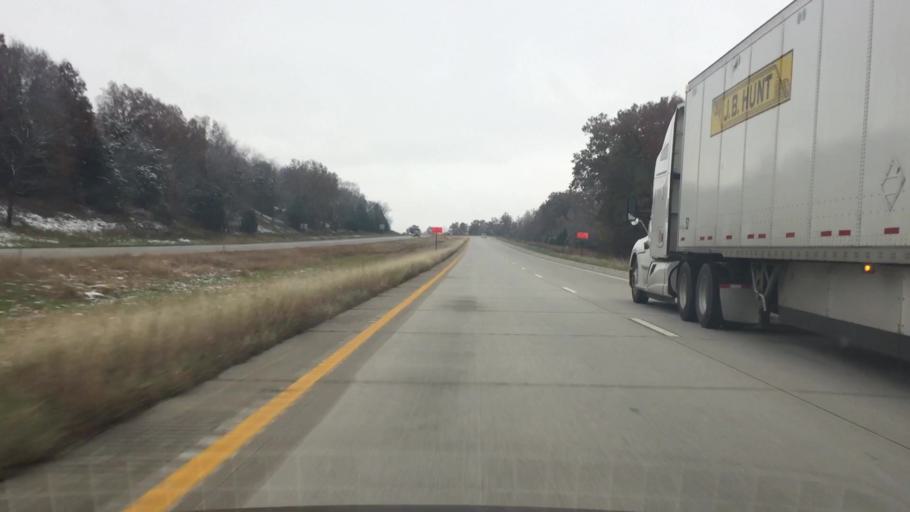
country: US
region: Missouri
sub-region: Henry County
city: Clinton
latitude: 38.2204
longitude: -93.7614
